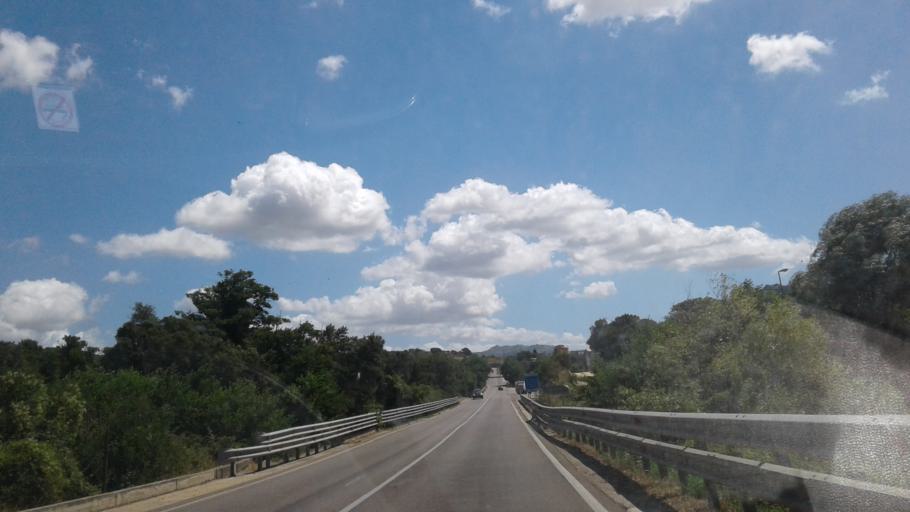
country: IT
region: Sardinia
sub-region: Provincia di Olbia-Tempio
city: Tempio Pausania
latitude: 40.9063
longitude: 9.1406
